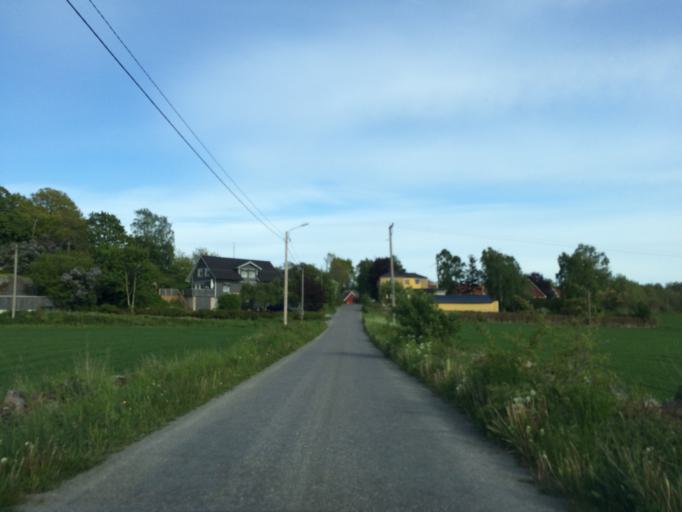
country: SE
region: Blekinge
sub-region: Karlshamns Kommun
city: Morrum
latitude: 56.1798
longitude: 14.7806
